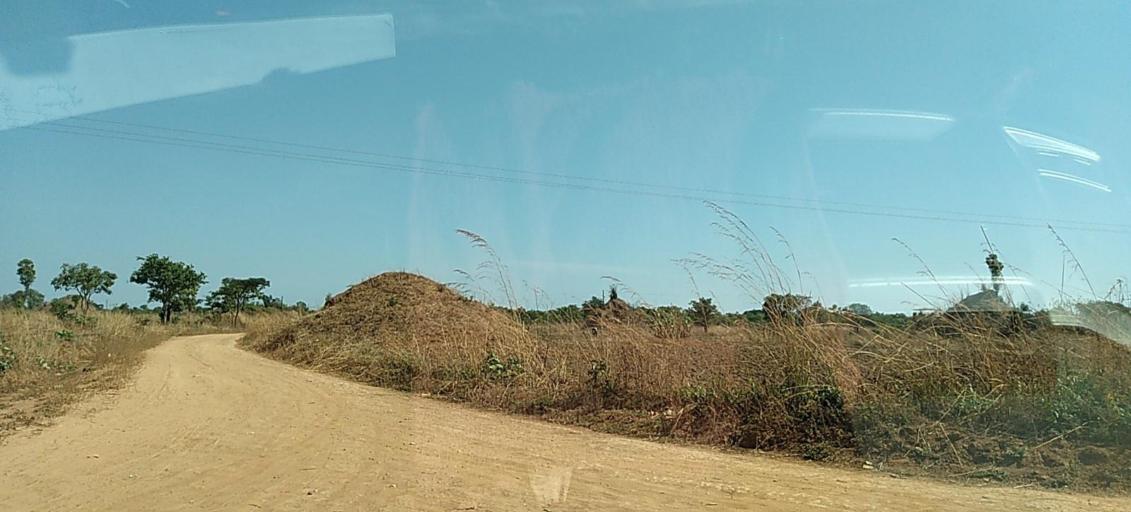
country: ZM
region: Copperbelt
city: Chililabombwe
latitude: -12.3534
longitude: 27.8837
